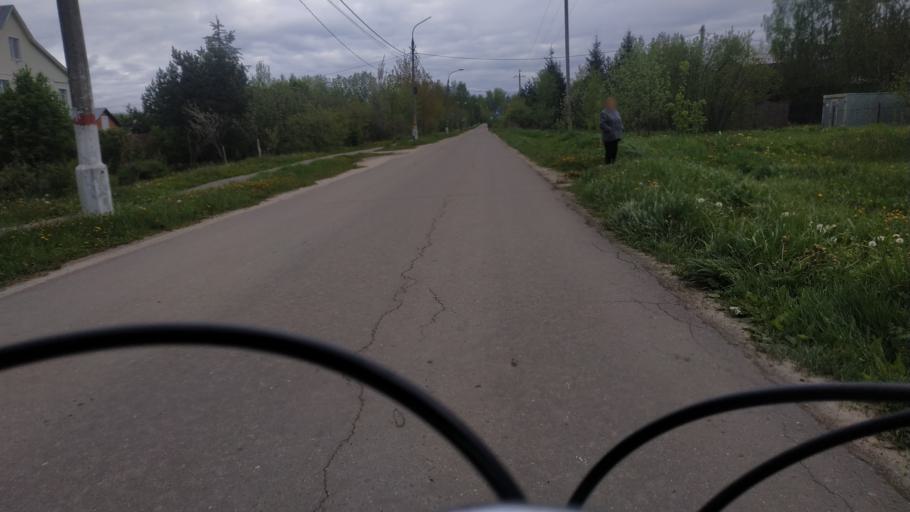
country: RU
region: Moskovskaya
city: Rechitsy
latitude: 55.6100
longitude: 38.5403
